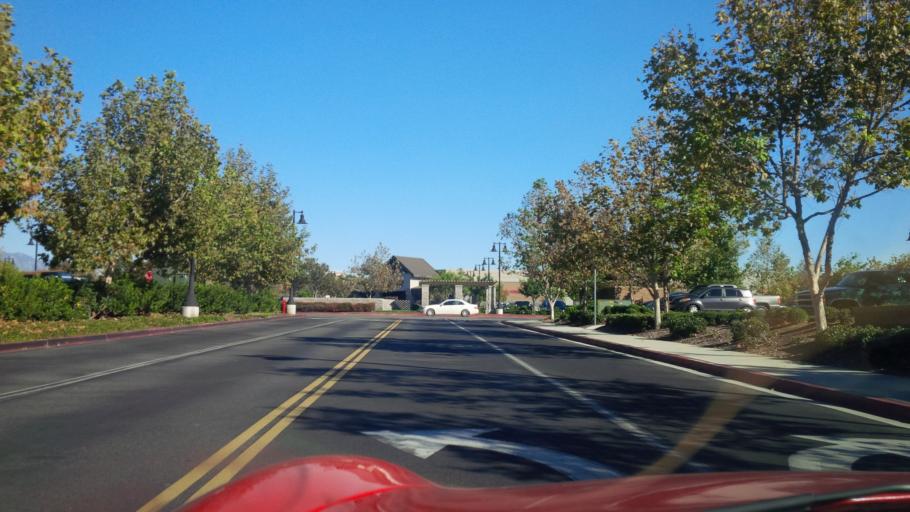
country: US
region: California
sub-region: Los Angeles County
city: Charter Oak
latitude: 34.1122
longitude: -117.8285
